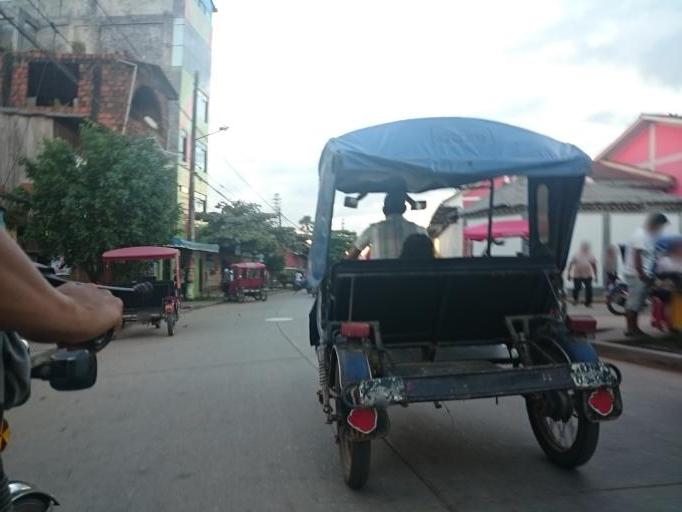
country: PE
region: Ucayali
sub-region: Provincia de Coronel Portillo
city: Pucallpa
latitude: -8.3801
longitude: -74.5392
